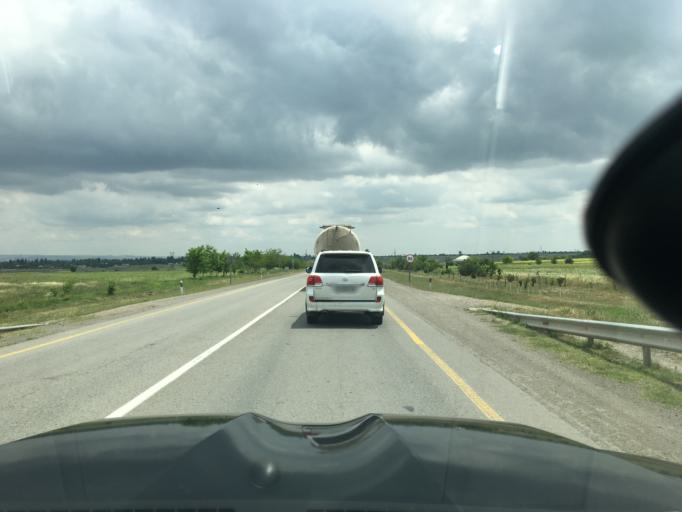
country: AZ
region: Tovuz
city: Qaraxanli
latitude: 41.0293
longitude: 45.6037
